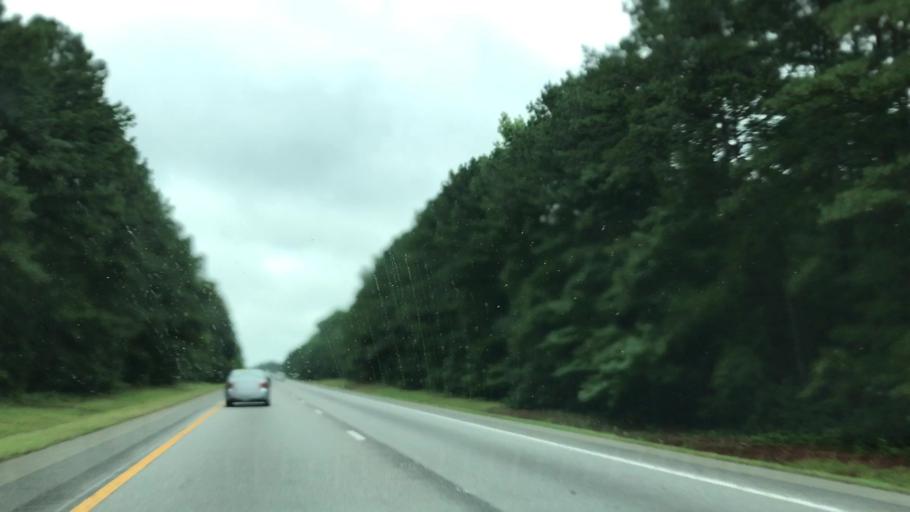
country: US
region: North Carolina
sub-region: Northampton County
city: Gaston
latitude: 36.4795
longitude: -77.6062
